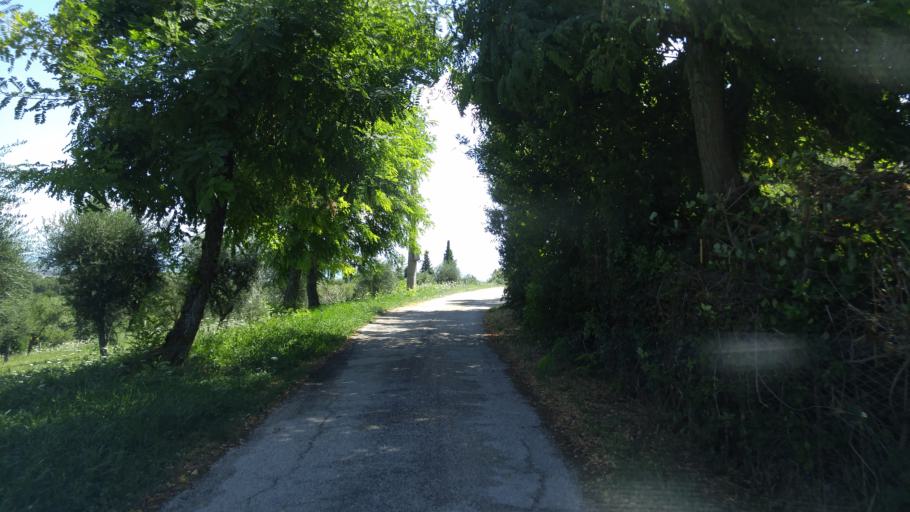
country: IT
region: The Marches
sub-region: Provincia di Pesaro e Urbino
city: Centinarola
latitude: 43.8196
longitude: 12.9801
